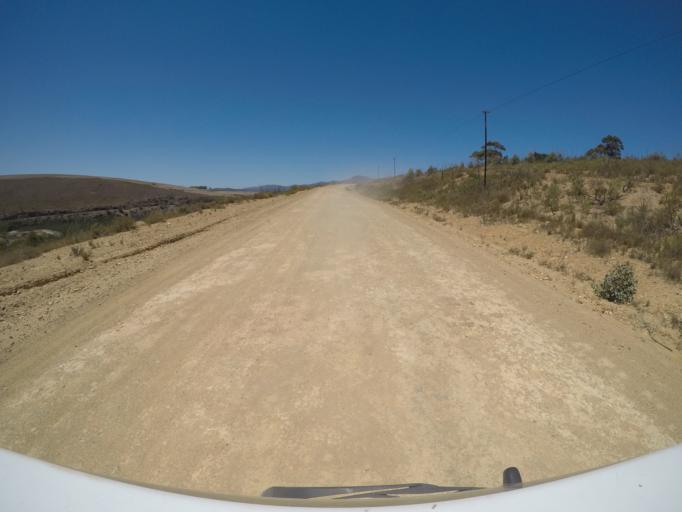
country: ZA
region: Western Cape
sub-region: Overberg District Municipality
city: Hermanus
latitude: -34.2198
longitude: 19.2045
